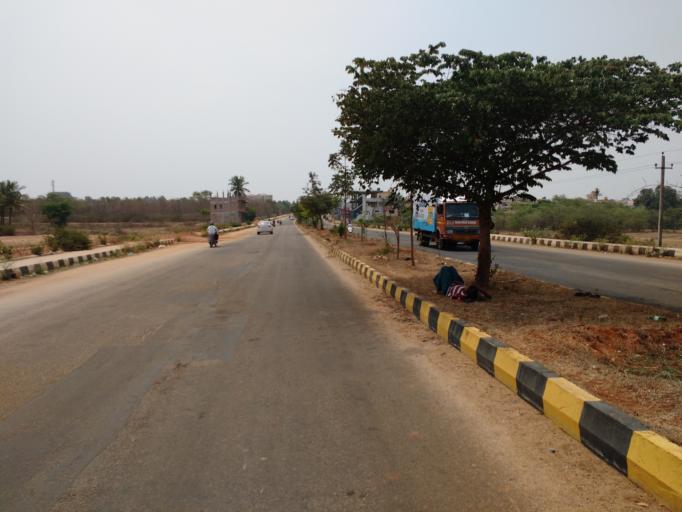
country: IN
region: Karnataka
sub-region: Hassan
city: Hassan
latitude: 13.0173
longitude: 76.1165
